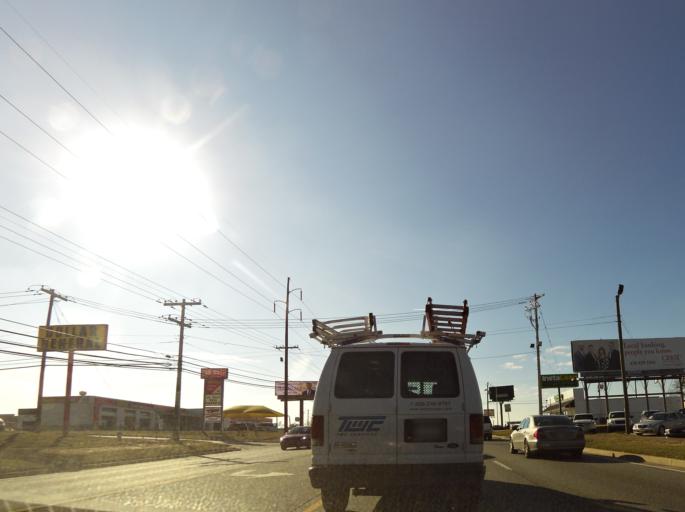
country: US
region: Georgia
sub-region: Houston County
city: Centerville
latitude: 32.6183
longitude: -83.6643
